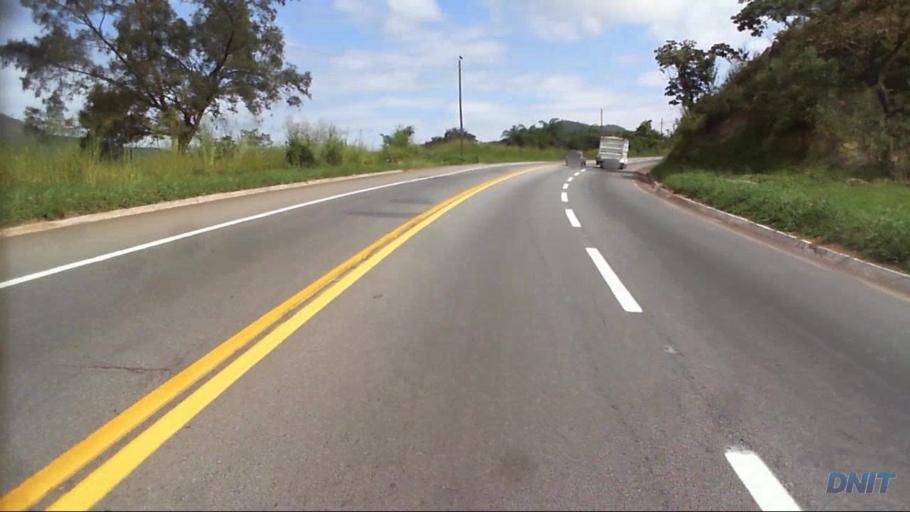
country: BR
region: Minas Gerais
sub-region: Santa Luzia
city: Santa Luzia
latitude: -19.8074
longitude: -43.7634
